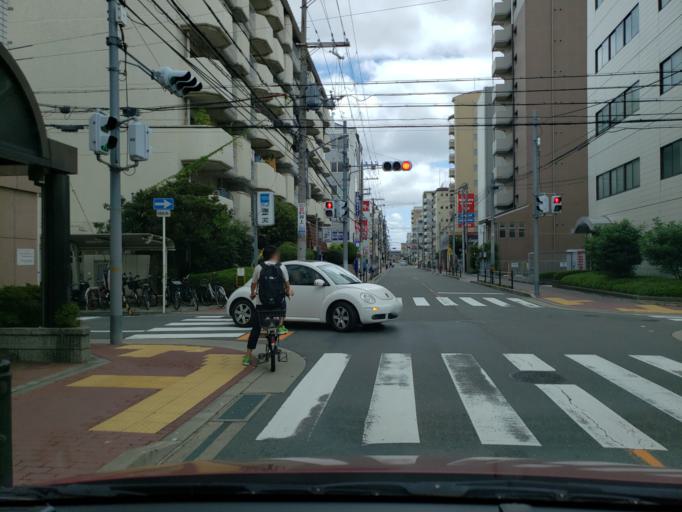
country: JP
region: Osaka
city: Suita
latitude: 34.7621
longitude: 135.5005
